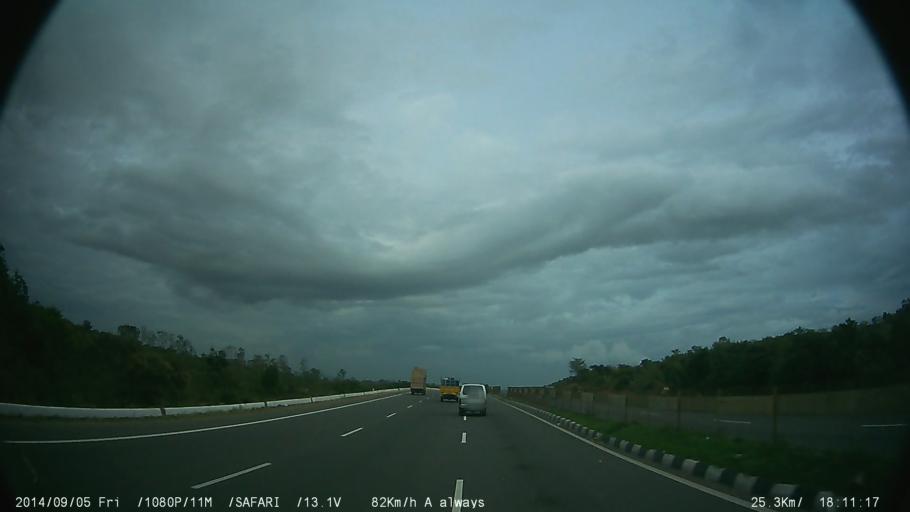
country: IN
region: Tamil Nadu
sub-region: Krishnagiri
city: Hosur
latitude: 12.7020
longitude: 77.9075
